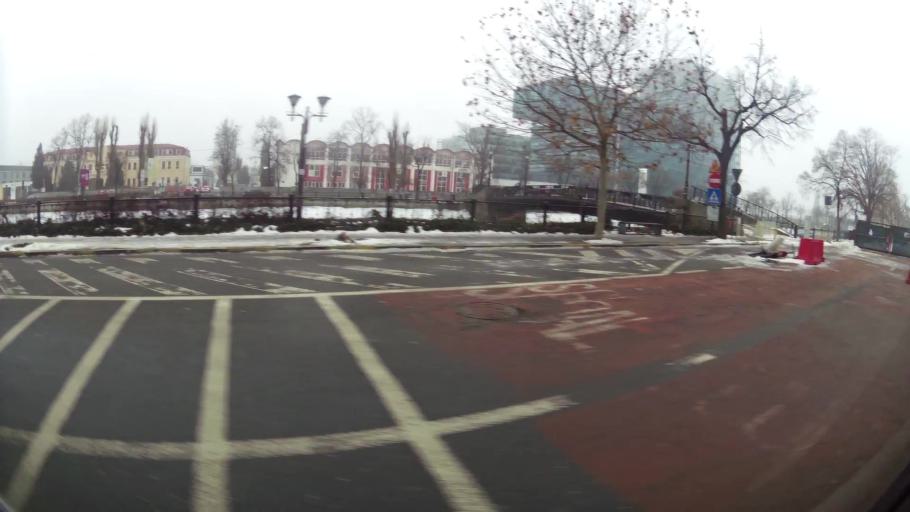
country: RO
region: Ilfov
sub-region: Comuna Chiajna
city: Rosu
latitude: 44.4459
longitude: 26.0474
